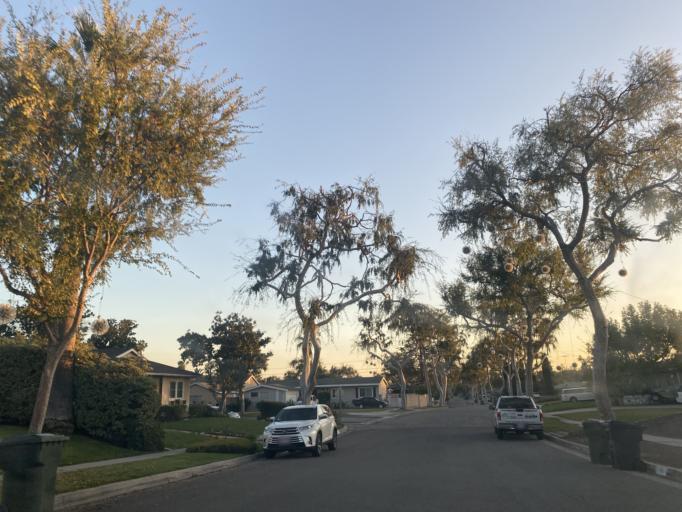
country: US
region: California
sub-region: Orange County
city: Fullerton
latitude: 33.8798
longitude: -117.9121
